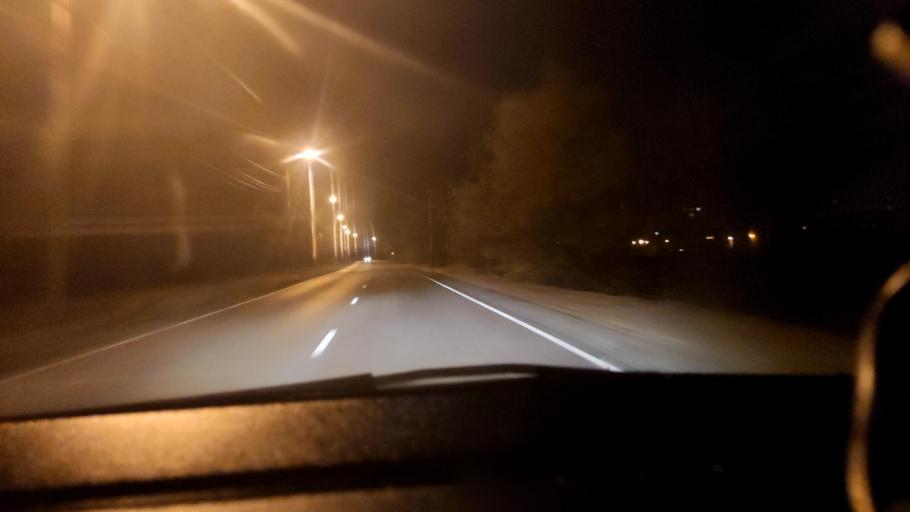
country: RU
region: Voronezj
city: Pridonskoy
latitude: 51.6282
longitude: 39.0817
